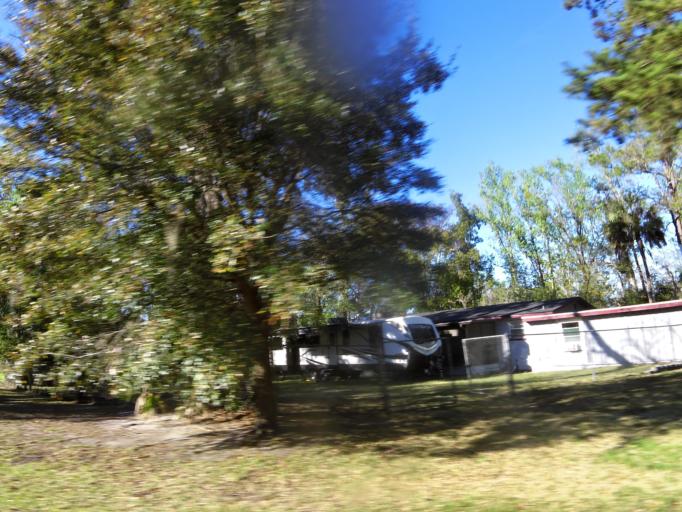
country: US
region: Florida
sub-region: Duval County
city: Jacksonville
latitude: 30.4011
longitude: -81.6753
